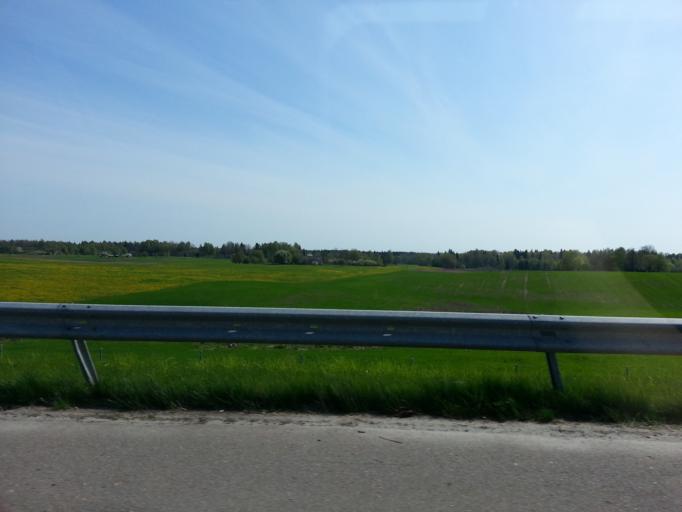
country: LT
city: Sirvintos
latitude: 55.1281
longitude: 24.8385
